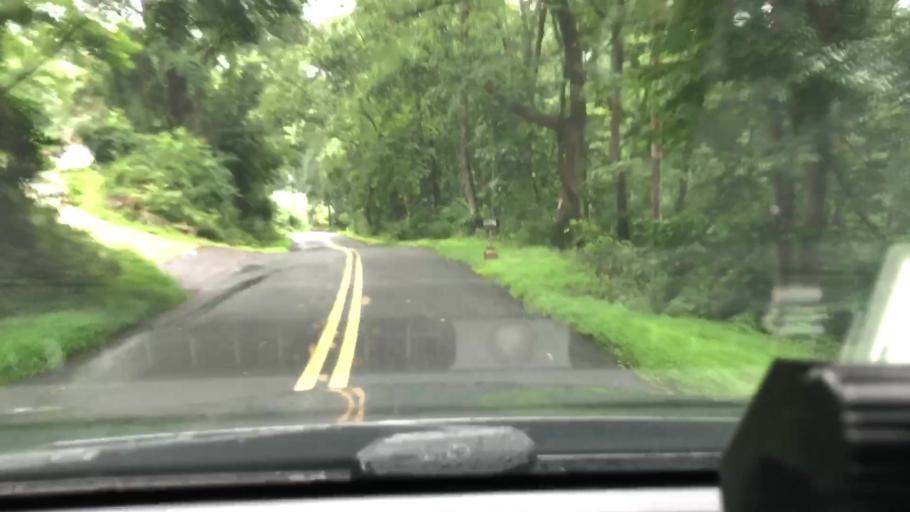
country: US
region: Pennsylvania
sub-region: Lehigh County
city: Macungie
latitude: 40.4780
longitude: -75.5489
